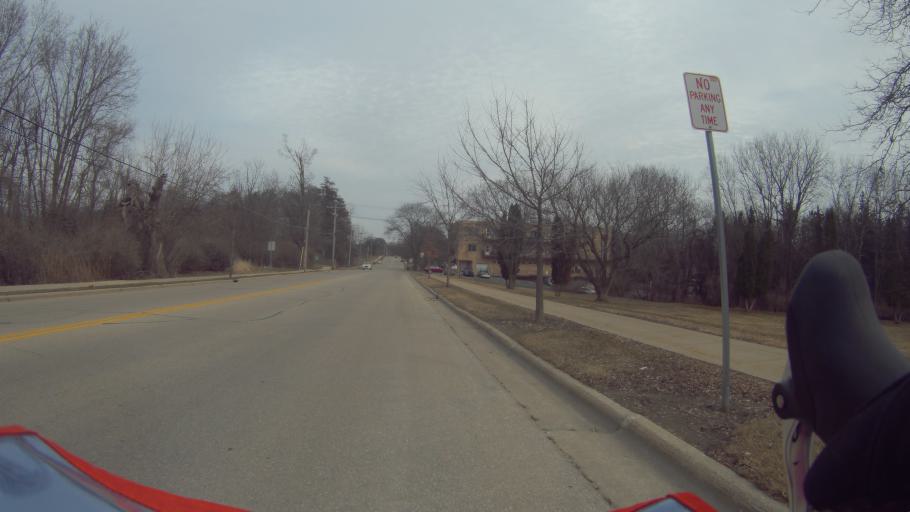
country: US
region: Wisconsin
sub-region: Dane County
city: Maple Bluff
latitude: 43.1338
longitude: -89.3944
